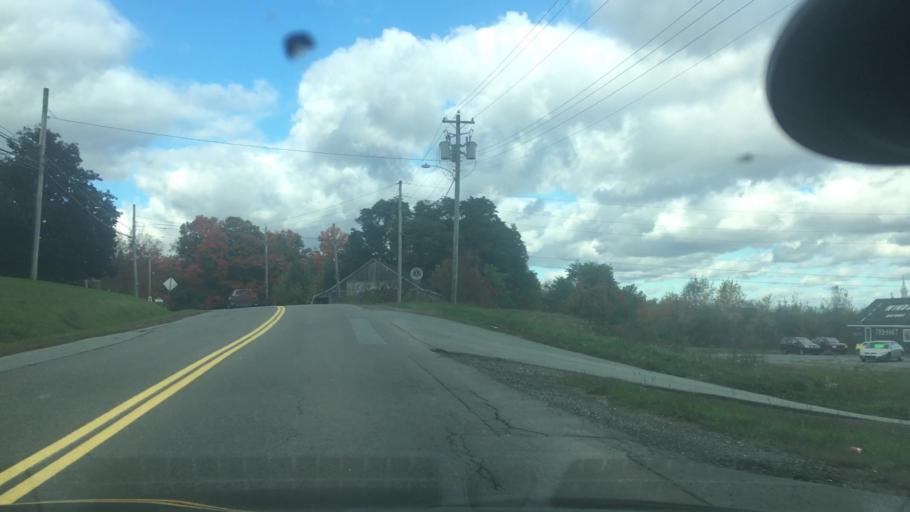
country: CA
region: Nova Scotia
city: Windsor
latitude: 44.9773
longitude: -64.1220
